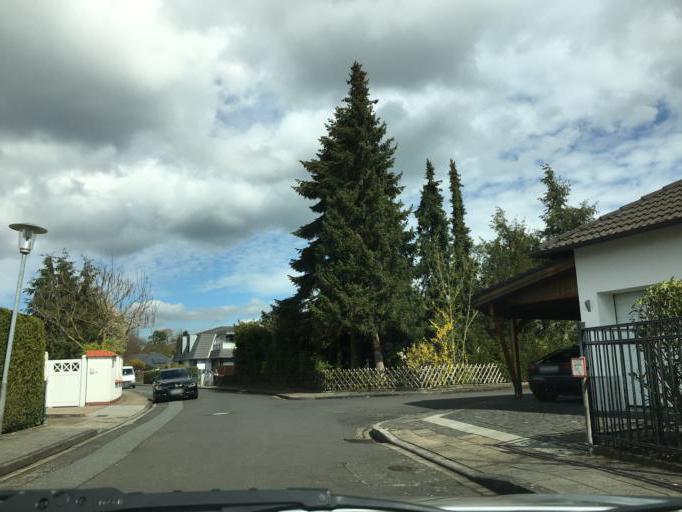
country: DE
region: Hesse
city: Obertshausen
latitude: 50.0516
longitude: 8.8482
